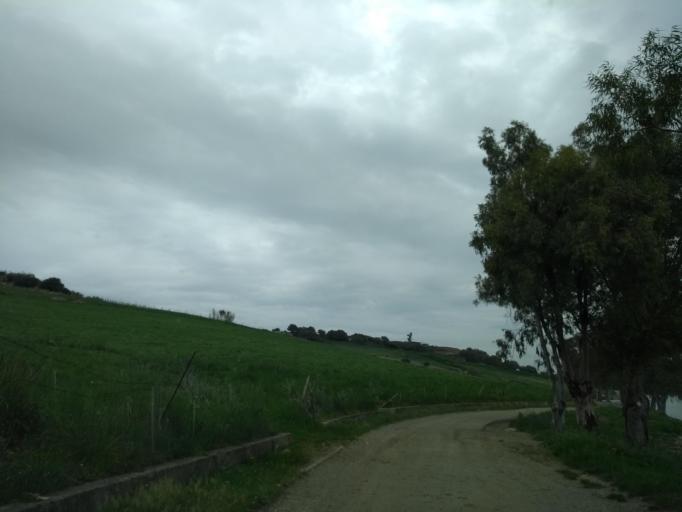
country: IT
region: Sicily
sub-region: Palermo
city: Partinico
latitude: 37.9920
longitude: 13.0823
